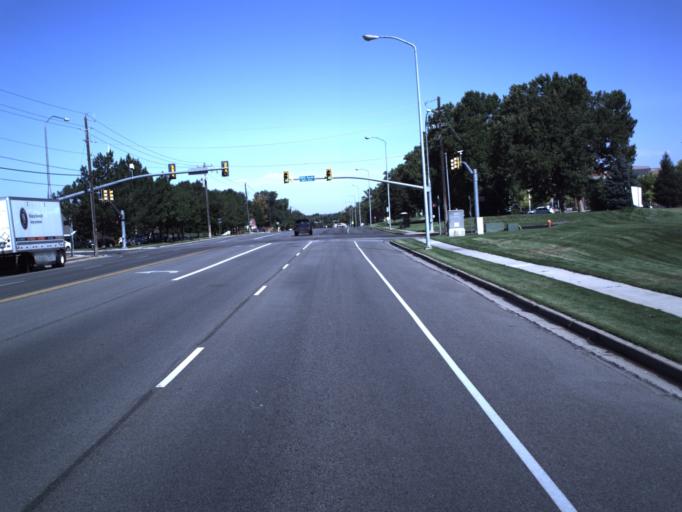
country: US
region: Utah
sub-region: Davis County
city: Kaysville
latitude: 41.0257
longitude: -111.9296
